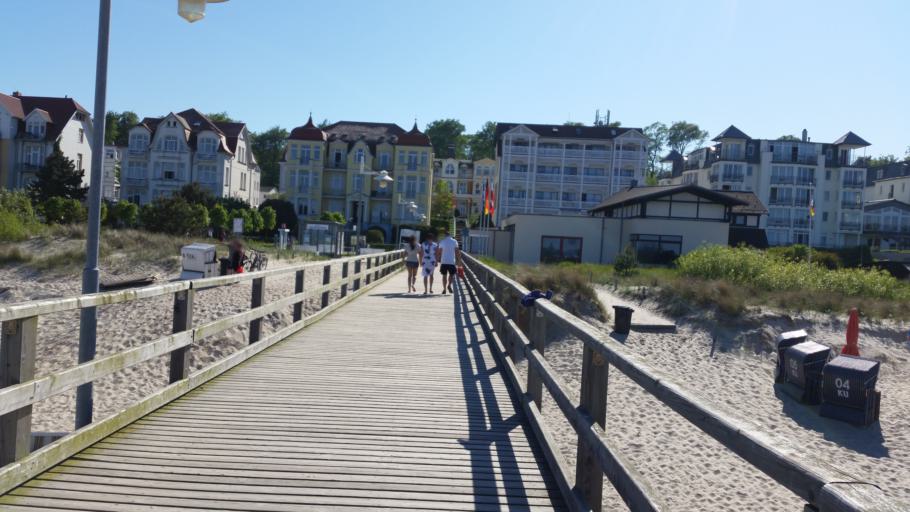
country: DE
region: Mecklenburg-Vorpommern
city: Seebad Bansin
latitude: 53.9751
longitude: 14.1436
